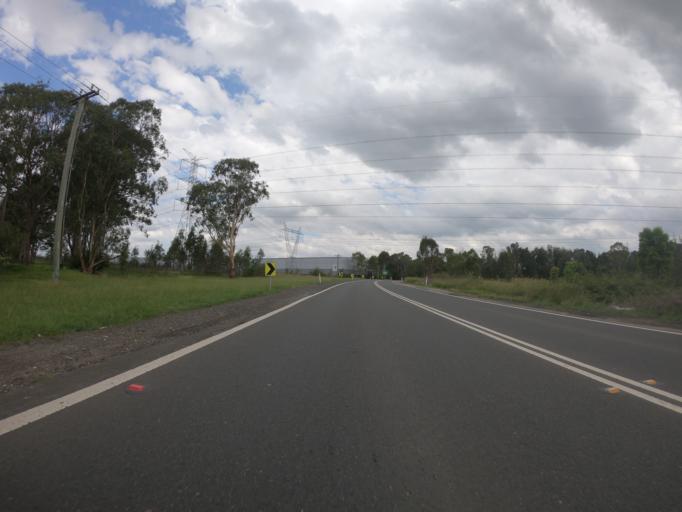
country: AU
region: New South Wales
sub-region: Blacktown
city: Mount Druitt
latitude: -33.8116
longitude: 150.7753
